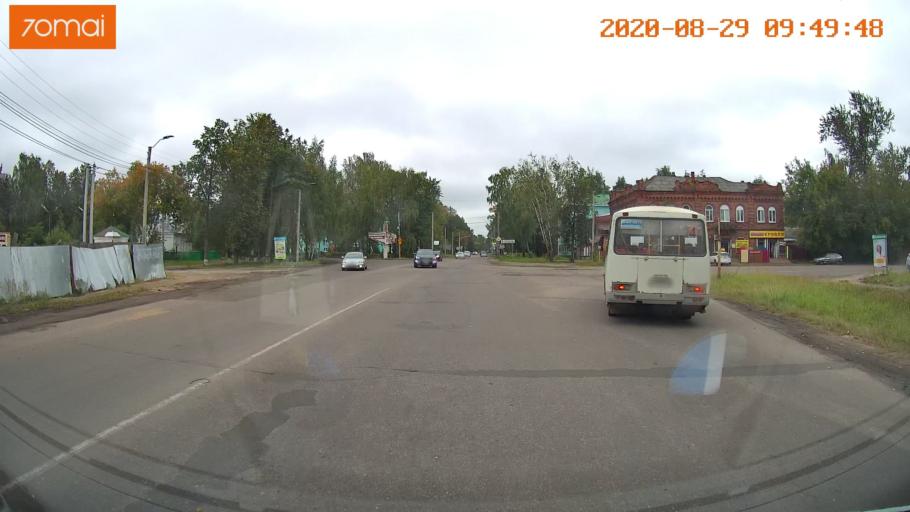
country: RU
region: Ivanovo
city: Kineshma
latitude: 57.4393
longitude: 42.1874
